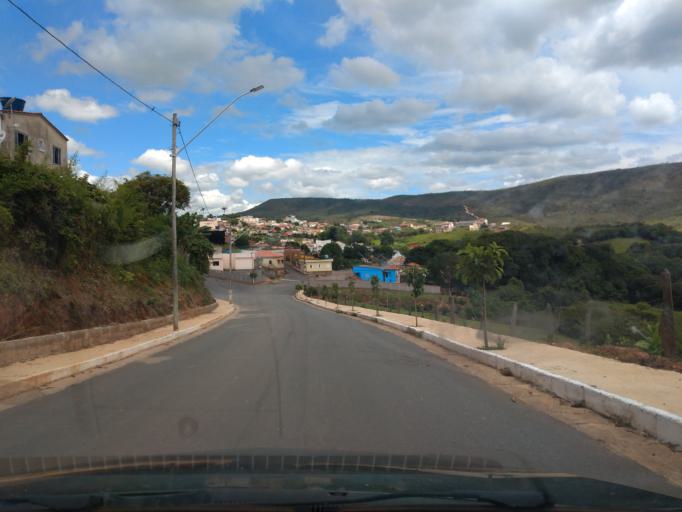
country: BR
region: Minas Gerais
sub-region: Lavras
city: Lavras
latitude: -21.5110
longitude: -44.9089
